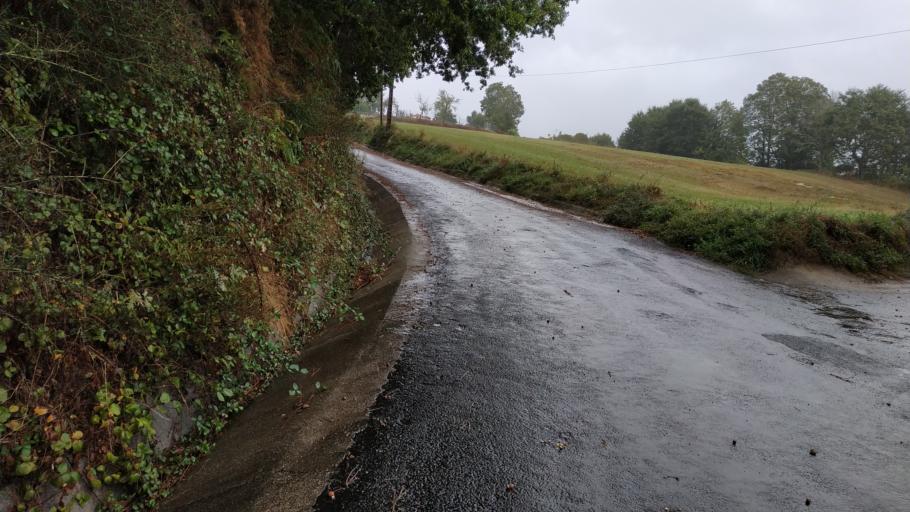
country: ES
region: Galicia
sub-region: Provincia da Coruna
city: Negreira
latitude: 42.9077
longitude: -8.7429
